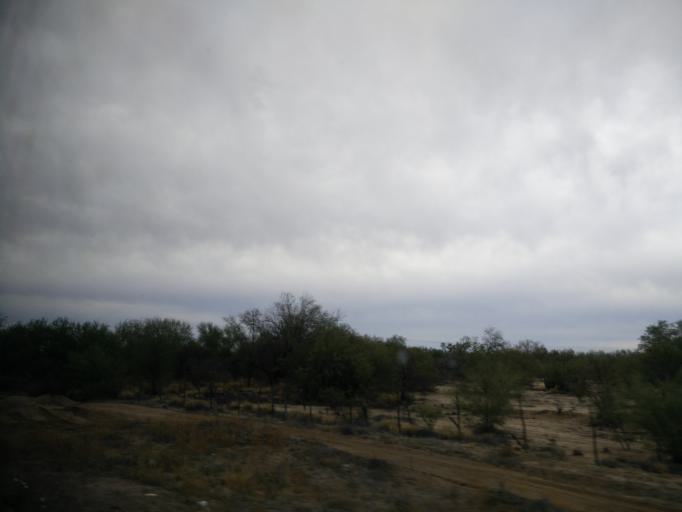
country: MX
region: Sonora
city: Hermosillo
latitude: 28.6935
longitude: -110.9888
